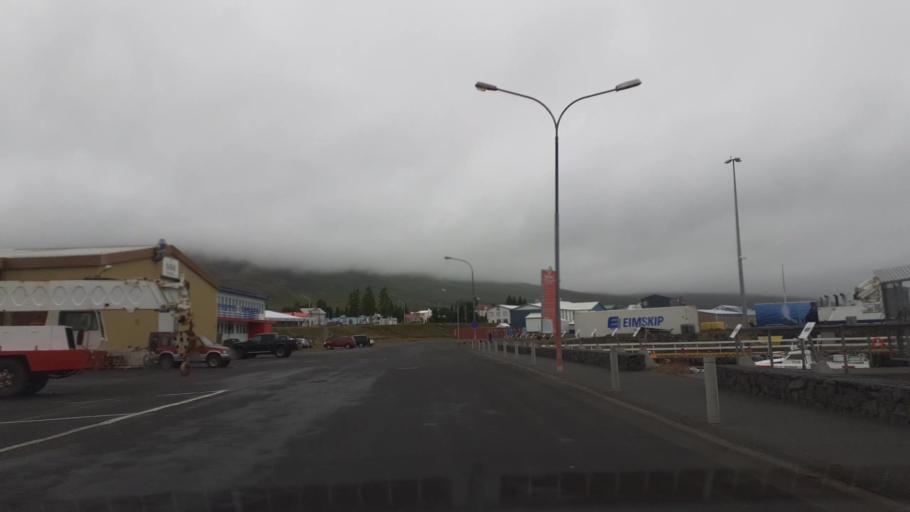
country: IS
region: Northeast
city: Dalvik
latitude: 65.9716
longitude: -18.5284
